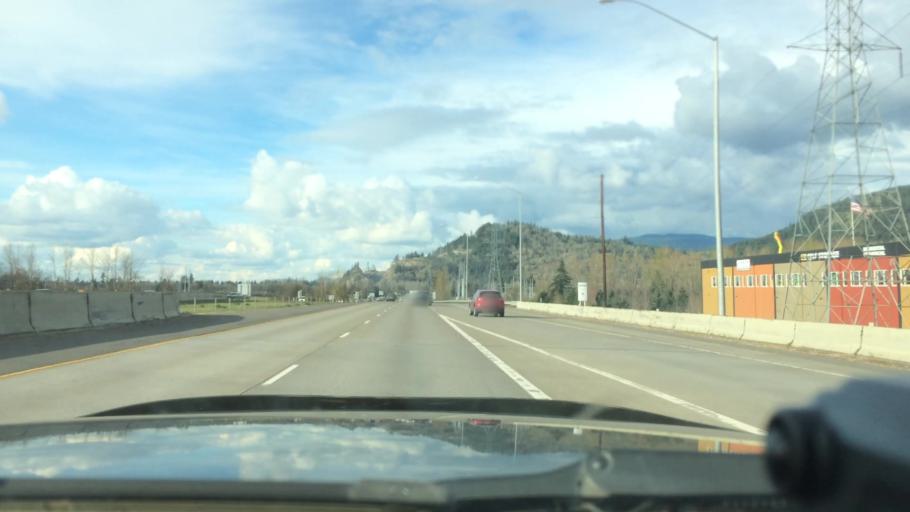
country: US
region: Oregon
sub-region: Lane County
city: Springfield
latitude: 44.0892
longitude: -123.0458
